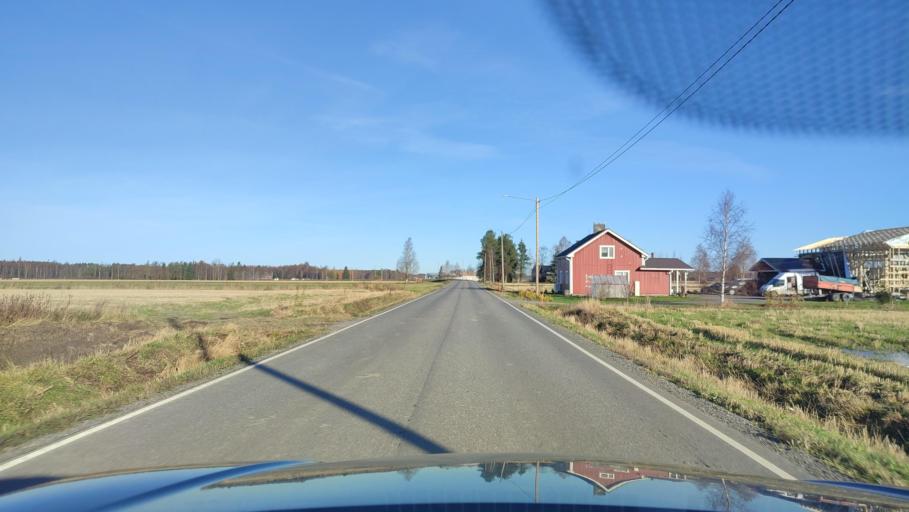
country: FI
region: Southern Ostrobothnia
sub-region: Suupohja
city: Karijoki
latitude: 62.2951
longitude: 21.7196
